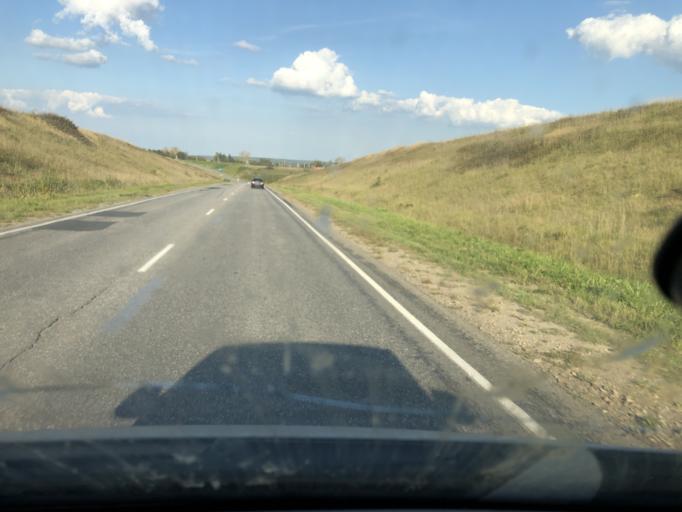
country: RU
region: Kaluga
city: Kozel'sk
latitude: 54.0866
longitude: 35.8324
